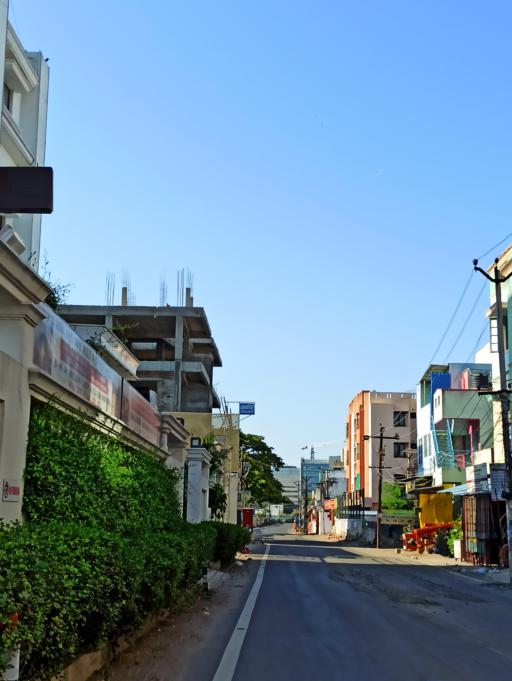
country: IN
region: Tamil Nadu
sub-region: Kancheepuram
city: Manappakkam
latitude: 13.0249
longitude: 80.1678
